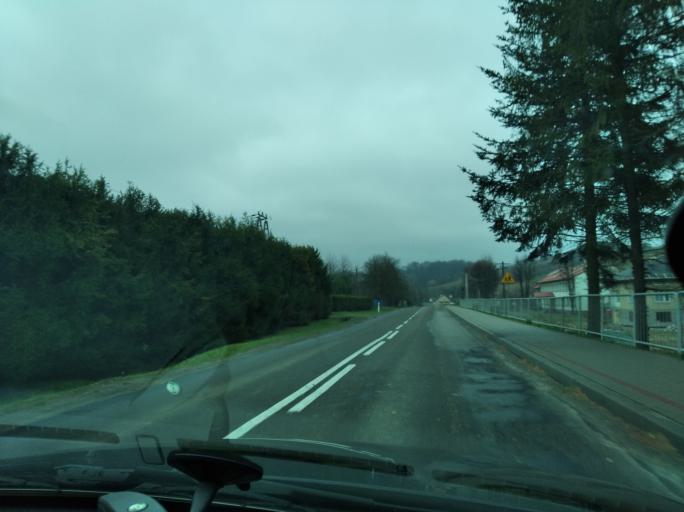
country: PL
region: Subcarpathian Voivodeship
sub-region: Powiat przeworski
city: Jawornik Polski
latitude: 49.8737
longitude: 22.2458
